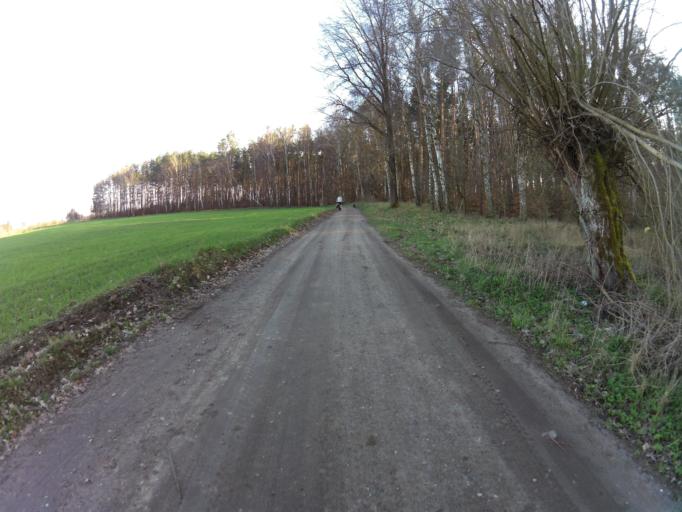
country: PL
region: West Pomeranian Voivodeship
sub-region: Powiat pyrzycki
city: Lipiany
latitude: 52.9562
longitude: 14.9295
